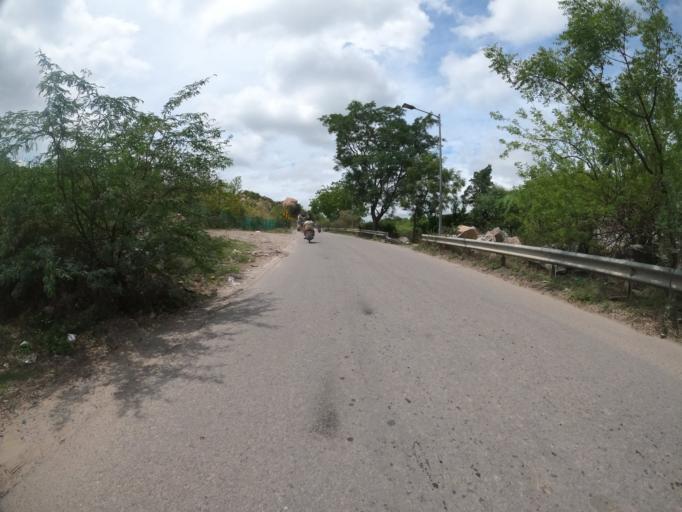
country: IN
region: Telangana
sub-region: Hyderabad
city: Hyderabad
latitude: 17.3155
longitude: 78.3720
